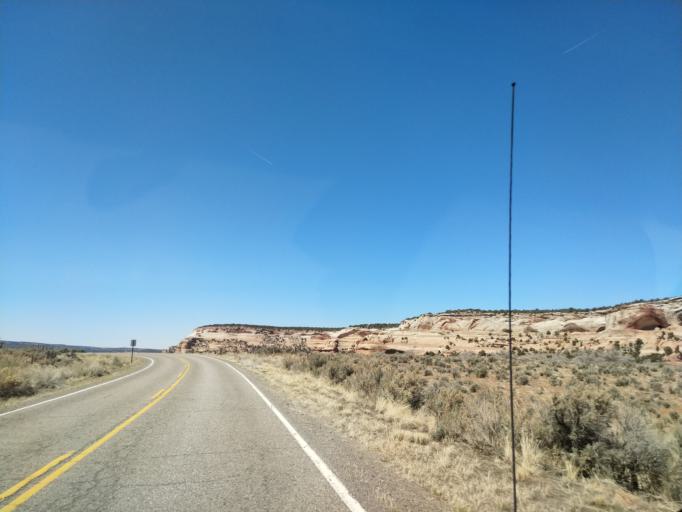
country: US
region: Colorado
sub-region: Mesa County
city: Loma
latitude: 38.9963
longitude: -108.8682
